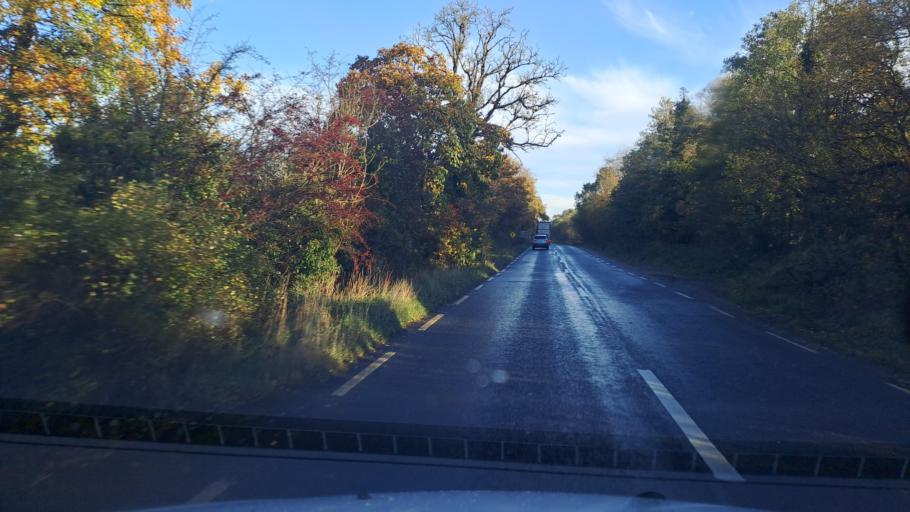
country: IE
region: Ulster
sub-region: An Cabhan
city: Cootehill
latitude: 54.0931
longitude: -7.0855
